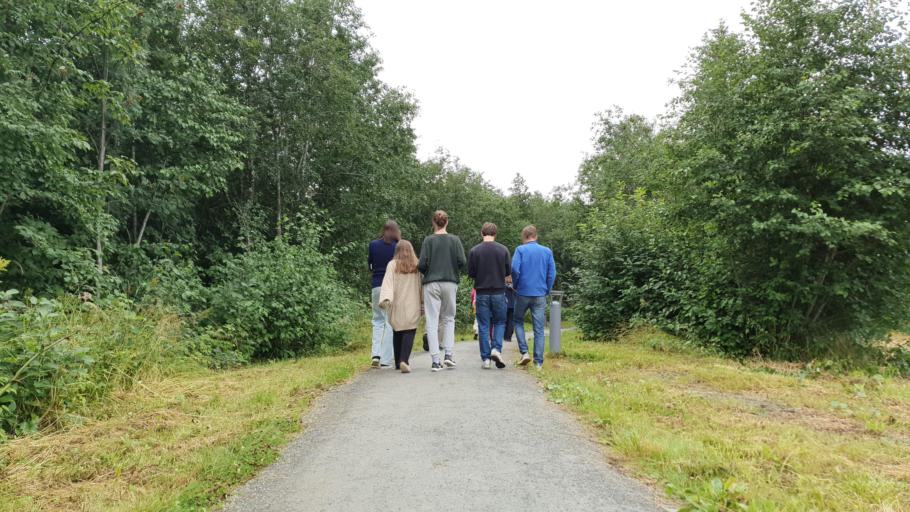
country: NO
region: Sor-Trondelag
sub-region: Selbu
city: Mebonden
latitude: 63.2316
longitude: 11.0254
